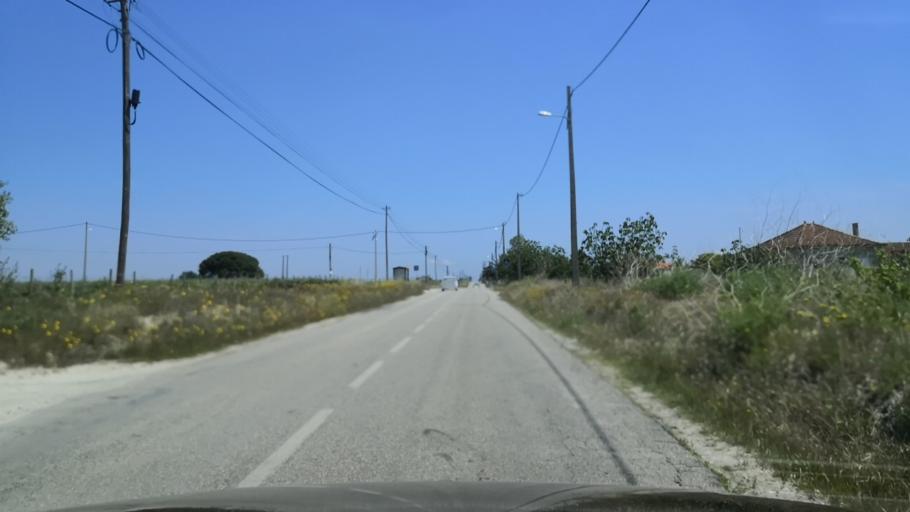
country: PT
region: Setubal
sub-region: Palmela
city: Palmela
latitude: 38.6026
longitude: -8.8123
